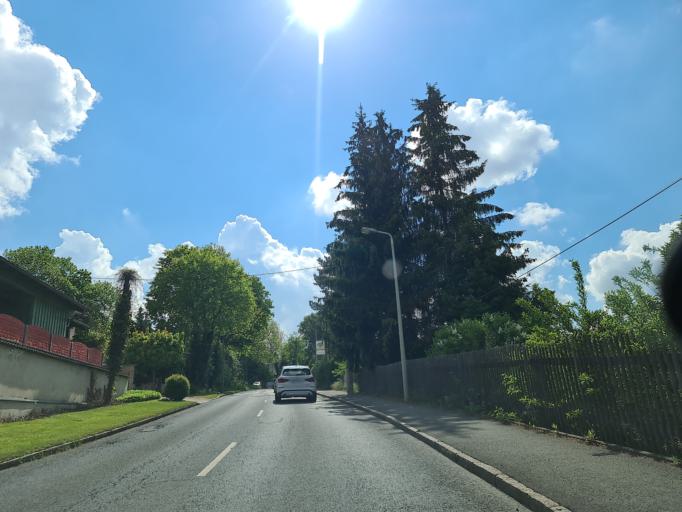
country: DE
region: Saxony
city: Wilkau-Hasslau
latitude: 50.6837
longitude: 12.4843
